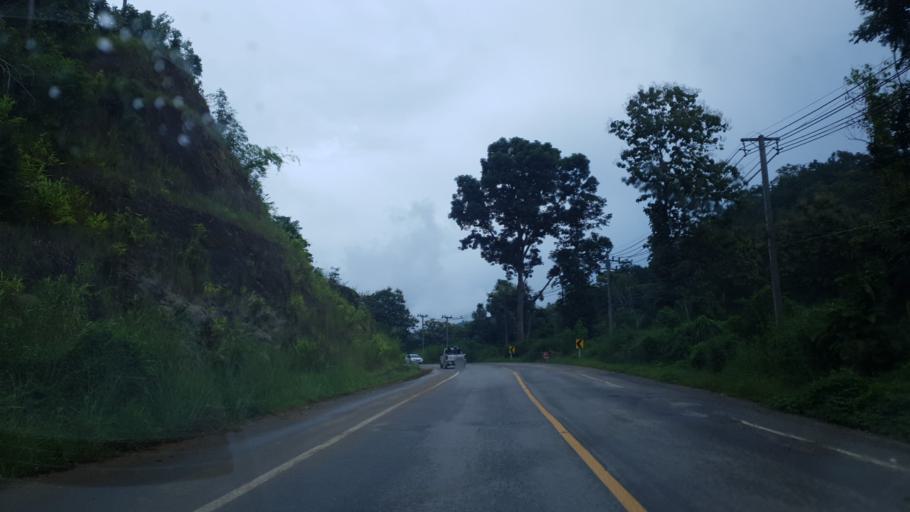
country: TH
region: Mae Hong Son
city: Ban Huai I Huak
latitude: 18.1382
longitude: 98.0028
